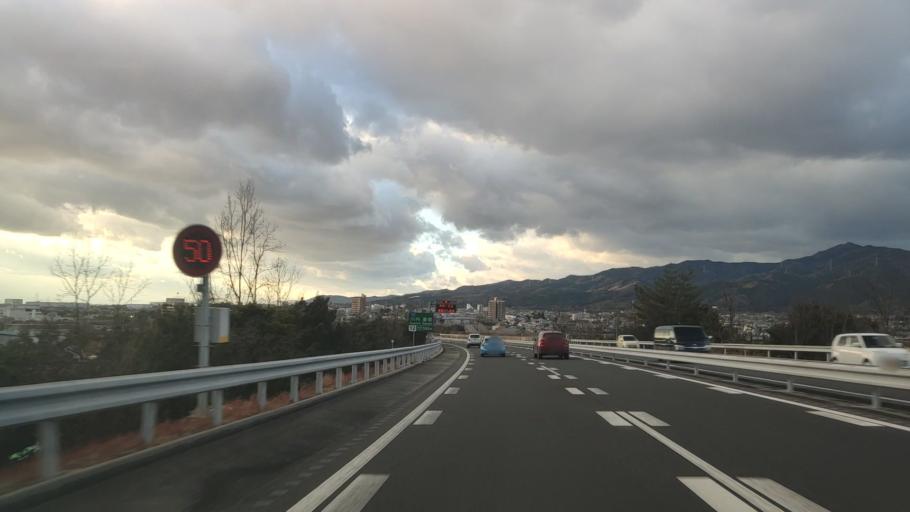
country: JP
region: Ehime
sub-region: Shikoku-chuo Shi
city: Matsuyama
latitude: 33.7932
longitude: 132.9122
